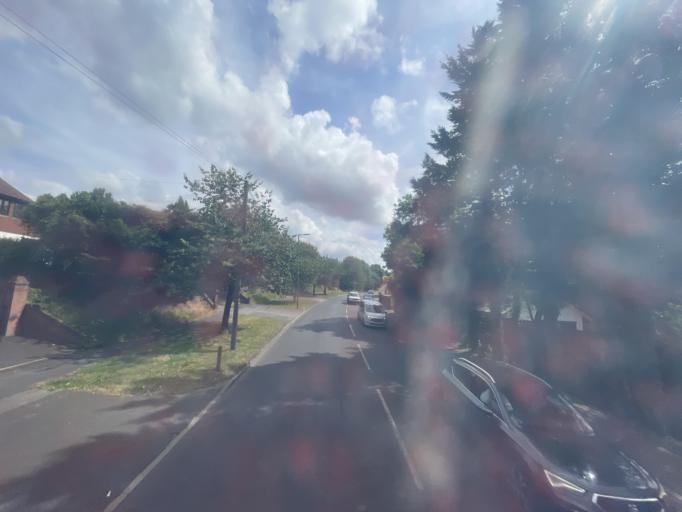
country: GB
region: England
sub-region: Kent
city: Biggin Hill
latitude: 51.3411
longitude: 0.0306
